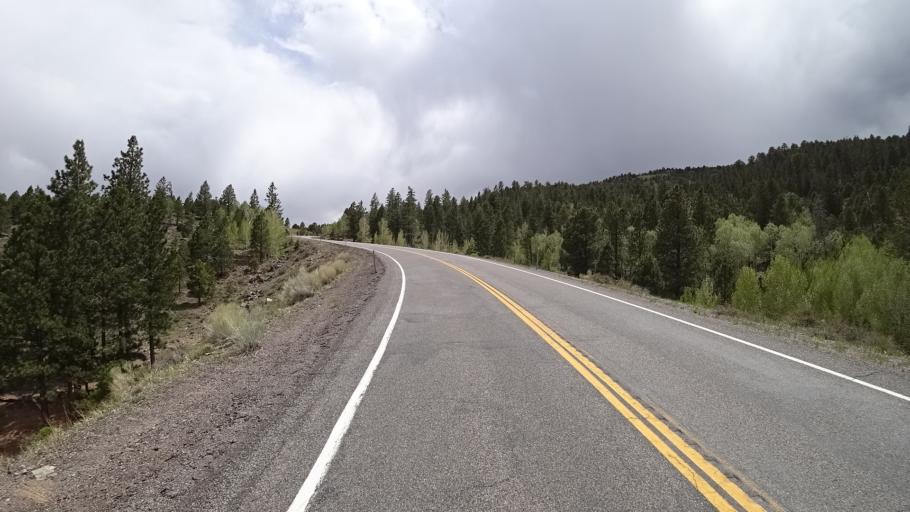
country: US
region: Utah
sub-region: Wayne County
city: Loa
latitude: 38.1583
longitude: -111.3336
